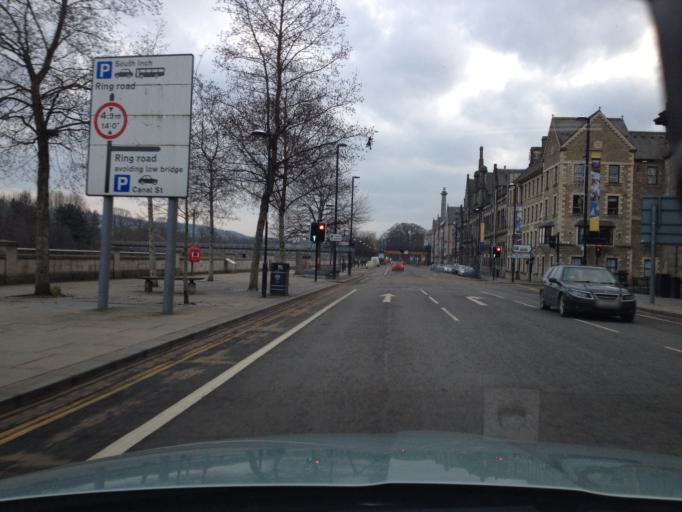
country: GB
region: Scotland
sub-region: Perth and Kinross
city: Perth
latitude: 56.3947
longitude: -3.4257
